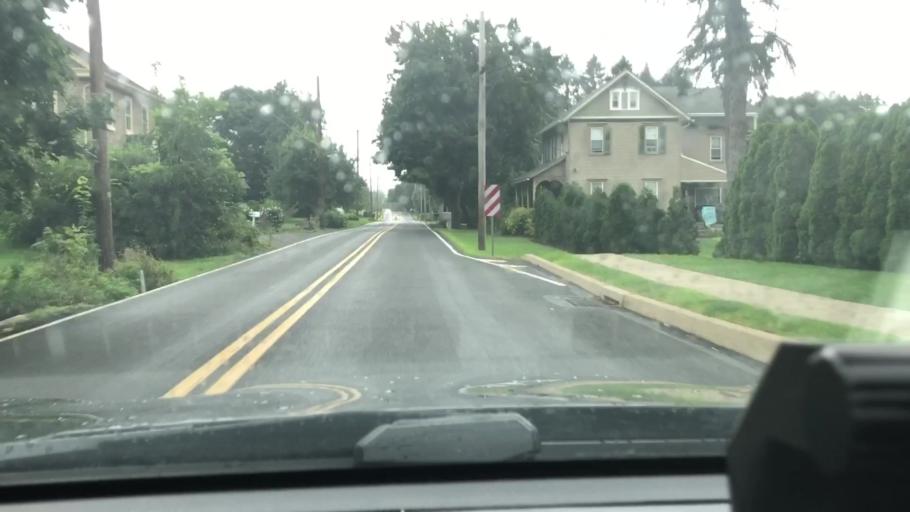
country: US
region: Pennsylvania
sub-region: Bucks County
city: Spinnerstown
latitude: 40.4353
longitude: -75.4319
